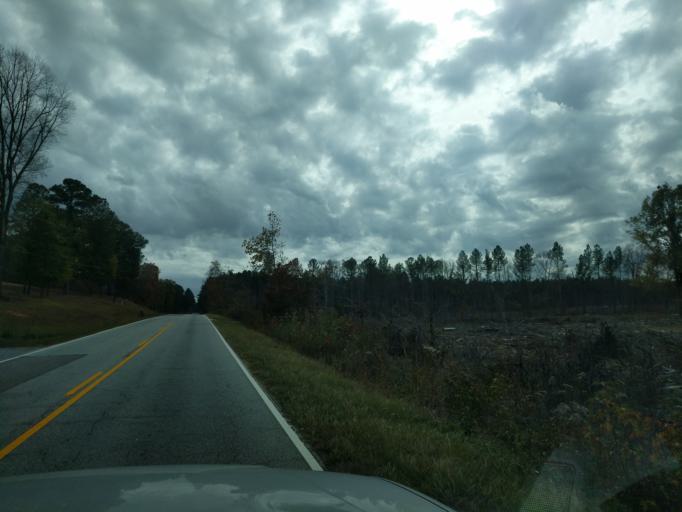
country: US
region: South Carolina
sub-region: Greenwood County
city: Ninety Six
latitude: 34.1712
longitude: -81.8614
